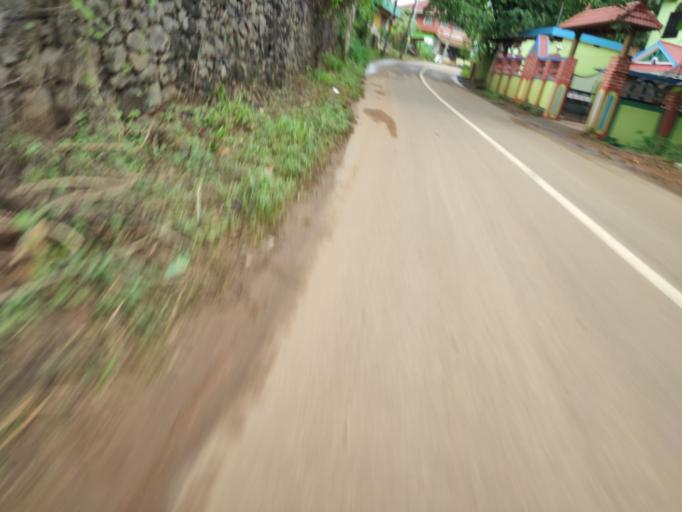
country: IN
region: Kerala
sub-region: Malappuram
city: Manjeri
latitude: 11.1460
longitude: 76.1463
